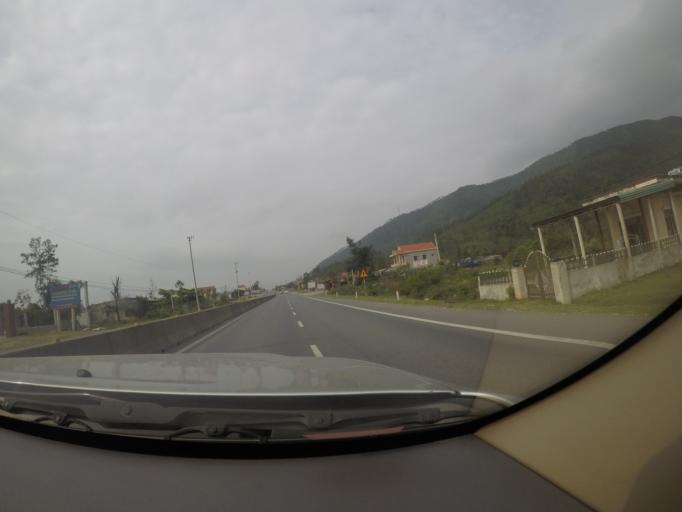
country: VN
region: Quang Binh
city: Ba Don
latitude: 17.9201
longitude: 106.4720
